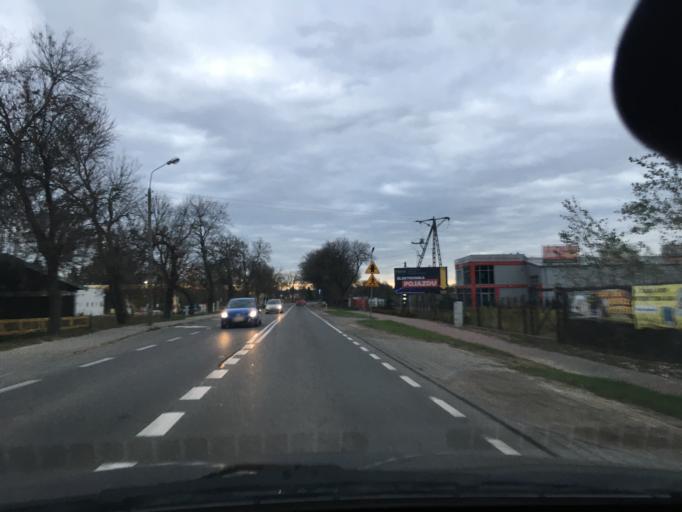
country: PL
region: Masovian Voivodeship
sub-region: Powiat piaseczynski
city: Lesznowola
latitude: 52.0964
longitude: 20.9207
